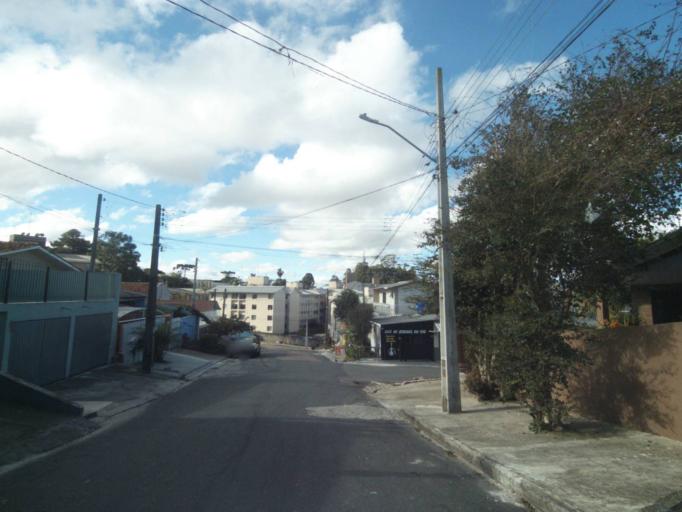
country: BR
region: Parana
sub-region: Sao Jose Dos Pinhais
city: Sao Jose dos Pinhais
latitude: -25.5313
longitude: -49.2834
